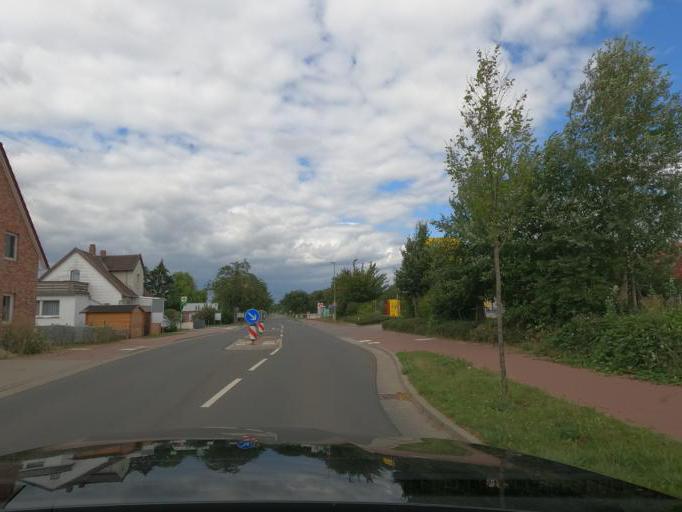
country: DE
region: Lower Saxony
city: Algermissen
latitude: 52.2578
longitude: 9.9635
